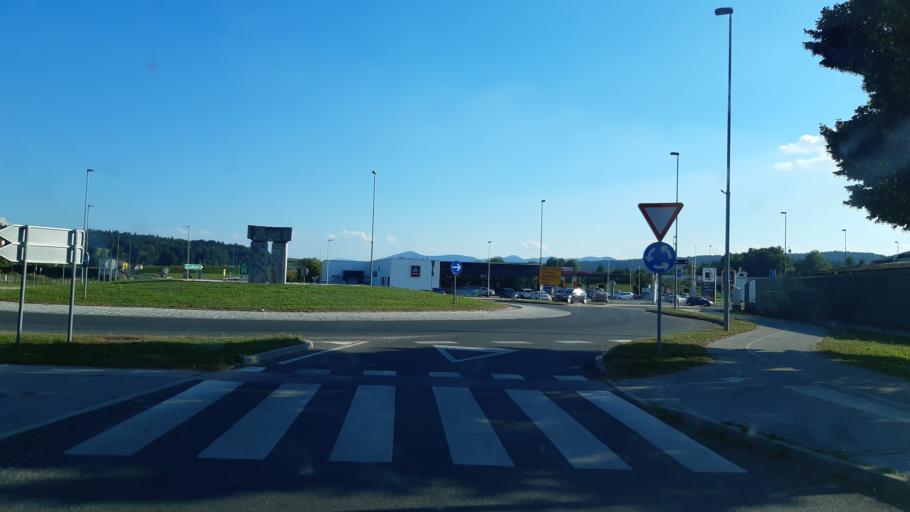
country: SI
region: Ivancna Gorica
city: Ivancna Gorica
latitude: 45.9373
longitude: 14.8052
